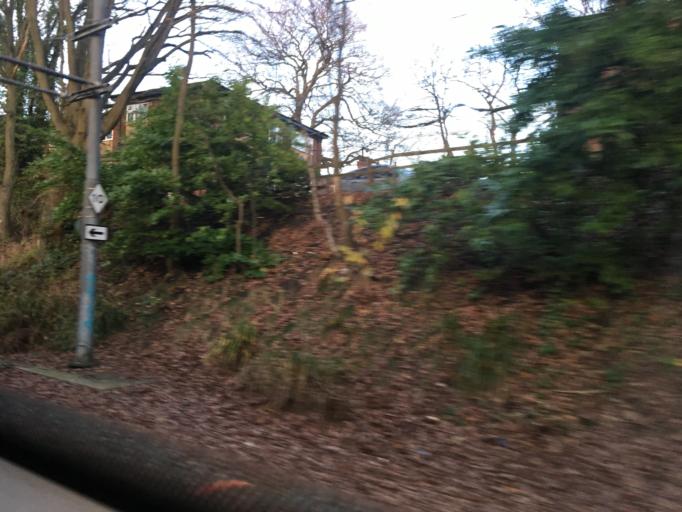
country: GB
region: England
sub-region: Manchester
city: Didsbury
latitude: 53.4232
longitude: -2.2353
